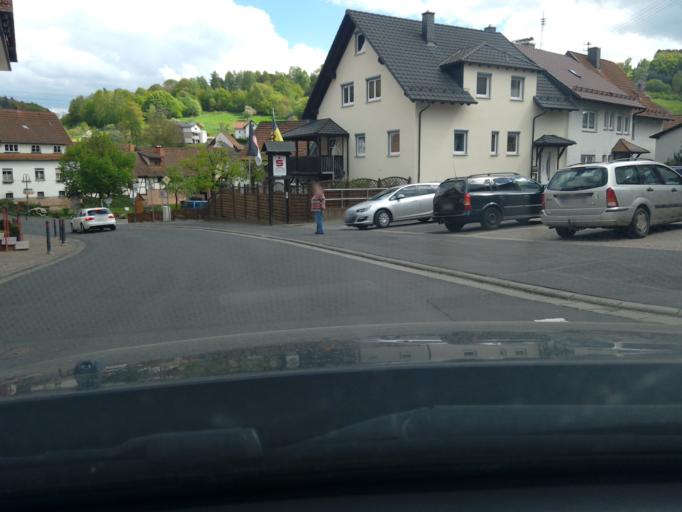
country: DE
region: Bavaria
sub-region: Regierungsbezirk Unterfranken
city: Frammersbach
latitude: 50.1274
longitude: 9.4774
